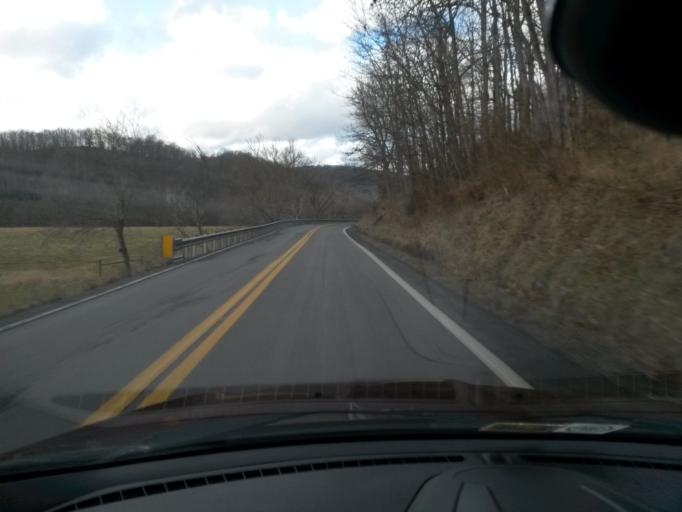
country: US
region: West Virginia
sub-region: Monroe County
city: Union
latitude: 37.5533
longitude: -80.5729
